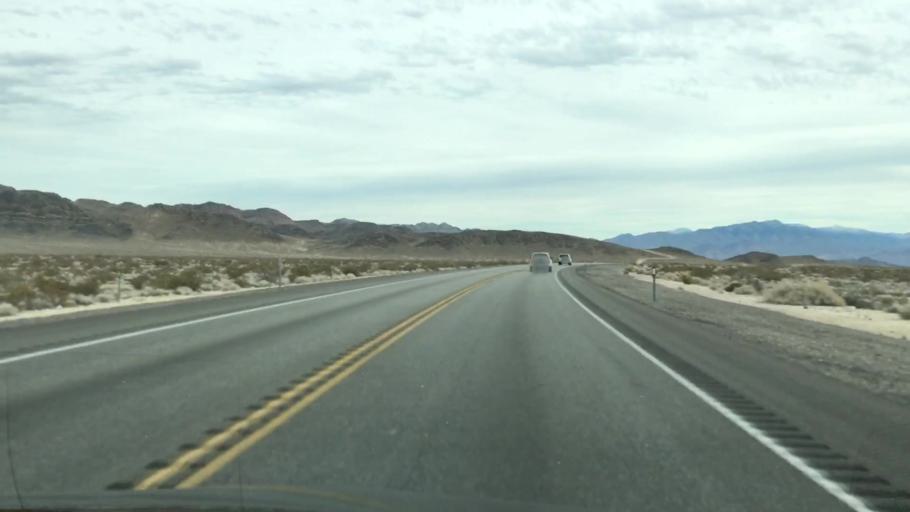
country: US
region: Nevada
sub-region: Nye County
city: Beatty
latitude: 36.6311
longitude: -116.3192
